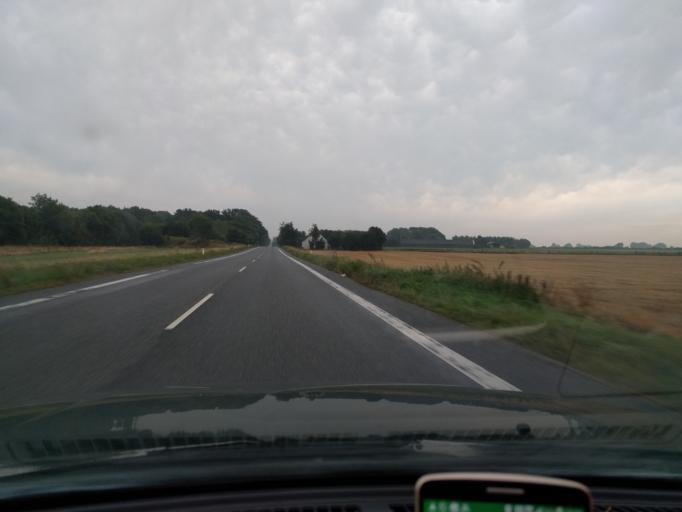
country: DK
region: Zealand
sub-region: Guldborgsund Kommune
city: Norre Alslev
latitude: 54.9295
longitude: 11.8719
